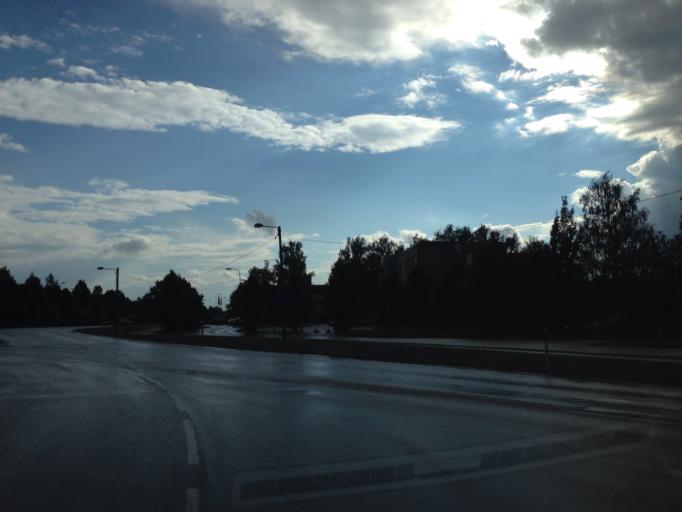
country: EE
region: Tartu
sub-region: Tartu linn
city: Tartu
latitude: 58.3576
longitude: 26.6816
